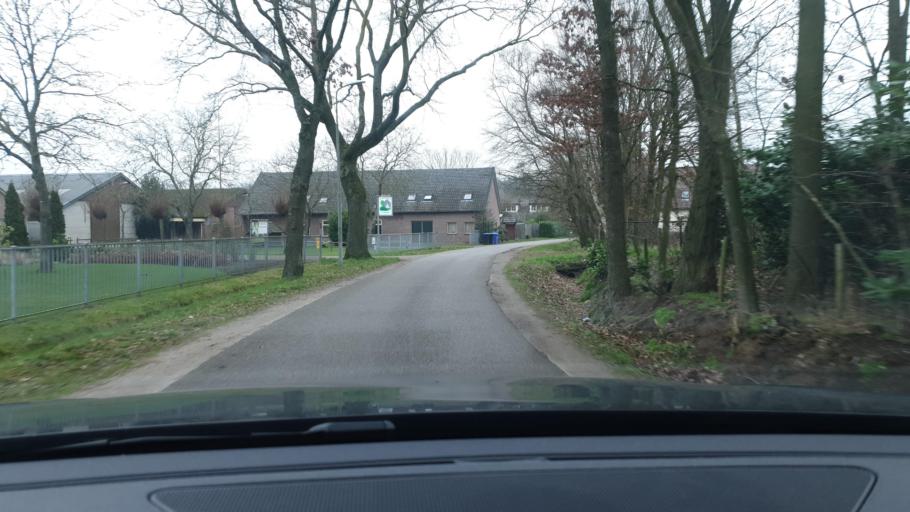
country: NL
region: North Brabant
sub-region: Gemeente Veldhoven
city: Oerle
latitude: 51.4057
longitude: 5.3689
